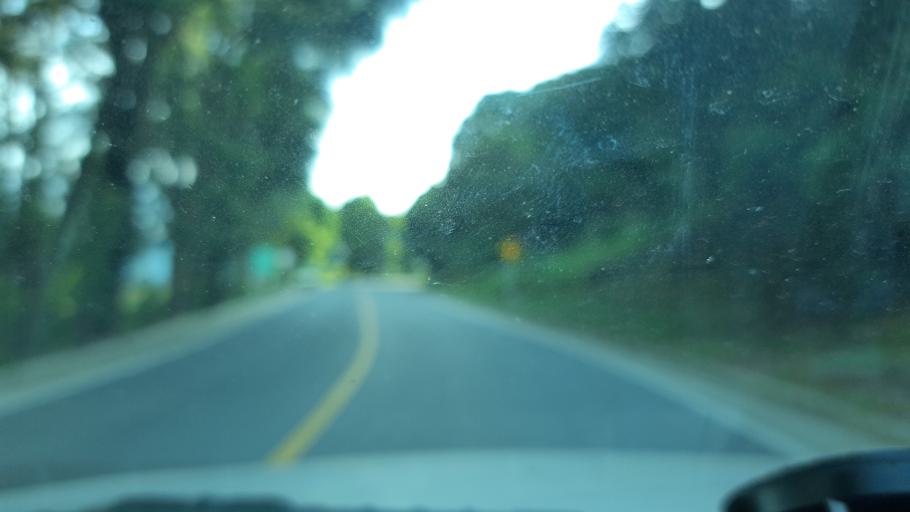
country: CO
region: Cundinamarca
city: Choconta
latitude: 5.0929
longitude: -73.6638
